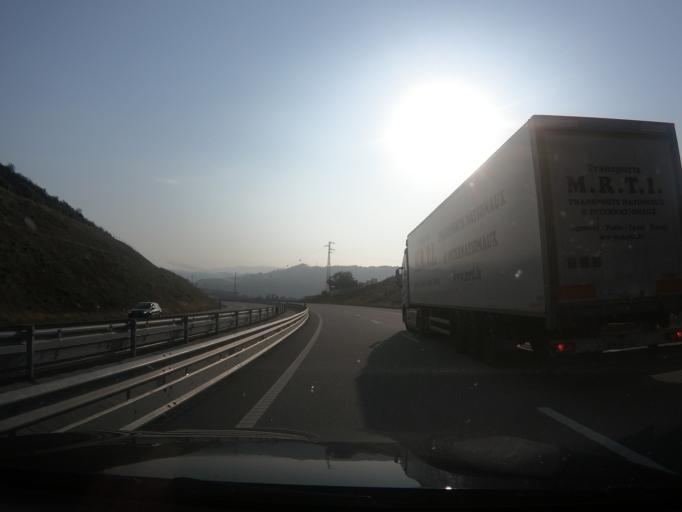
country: PT
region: Porto
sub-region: Amarante
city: Amarante
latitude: 41.2611
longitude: -8.0110
